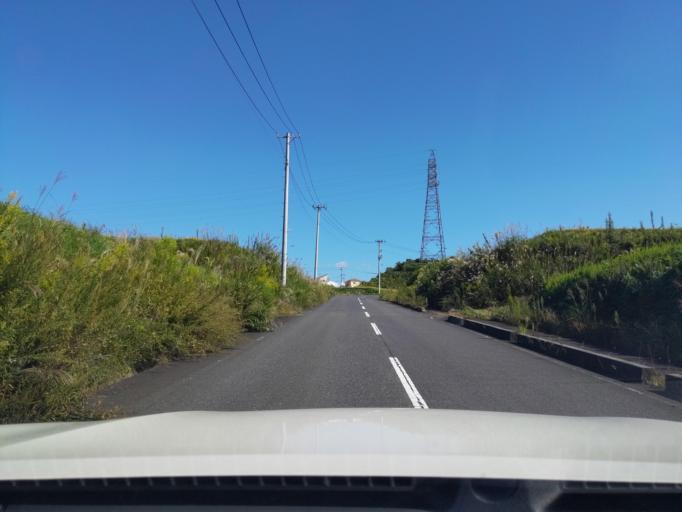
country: JP
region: Fukushima
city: Koriyama
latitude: 37.3851
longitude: 140.4303
